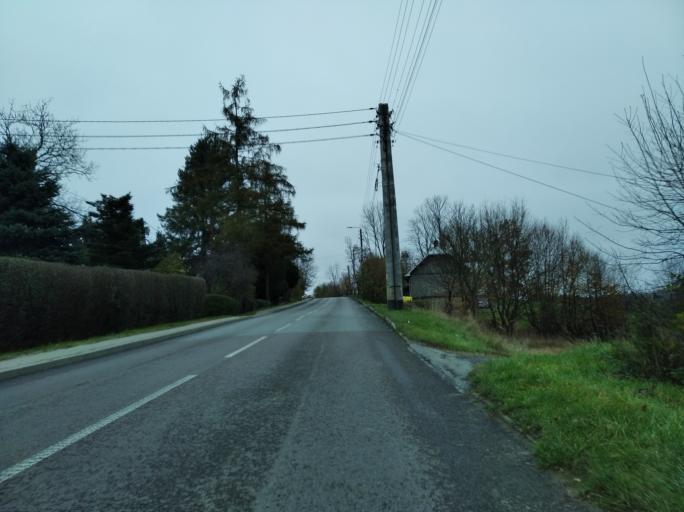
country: PL
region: Subcarpathian Voivodeship
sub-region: Krosno
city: Krosno
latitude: 49.7033
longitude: 21.7602
